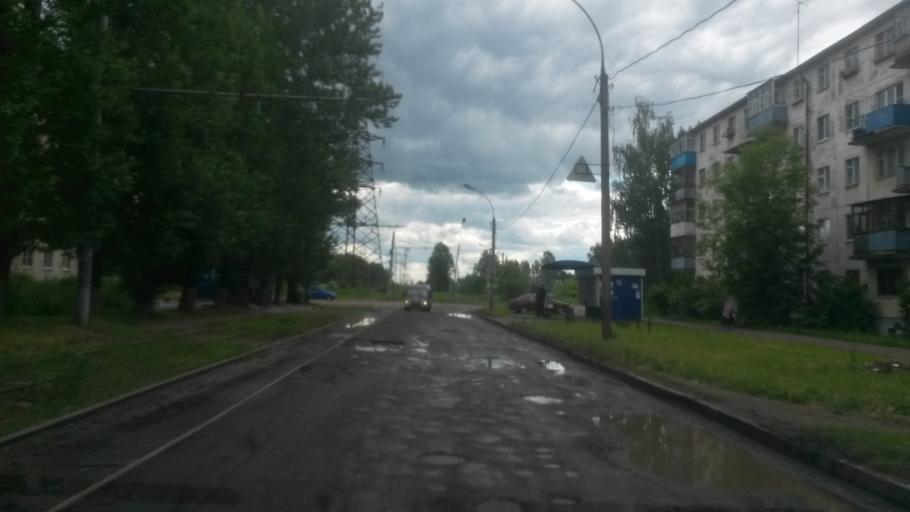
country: RU
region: Jaroslavl
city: Yaroslavl
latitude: 57.6837
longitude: 39.8098
